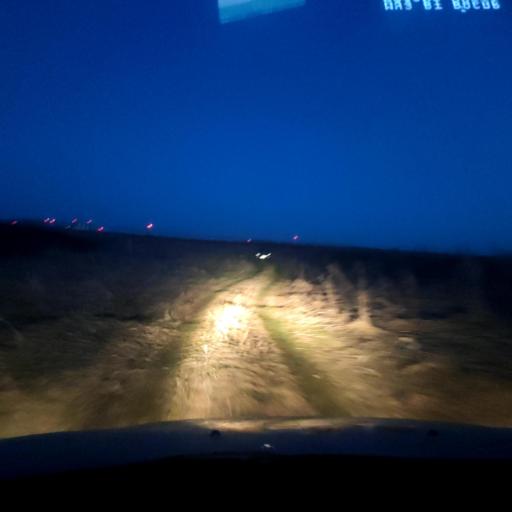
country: RU
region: Bashkortostan
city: Avdon
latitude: 54.5759
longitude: 55.8510
